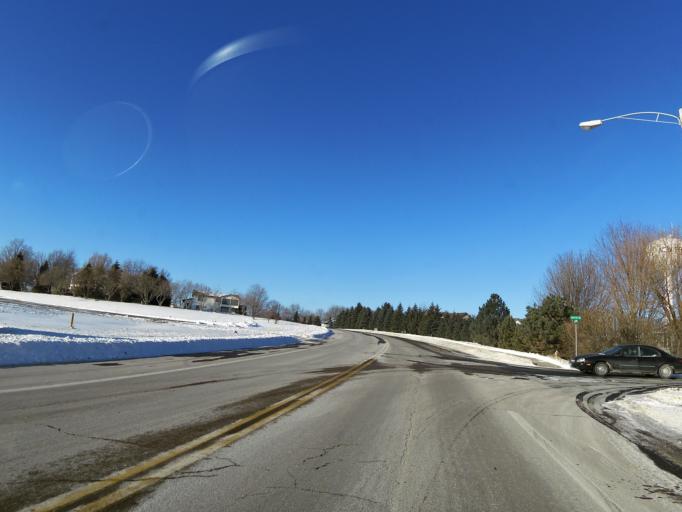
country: US
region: Minnesota
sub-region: Le Sueur County
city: New Prague
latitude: 44.5476
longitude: -93.5616
